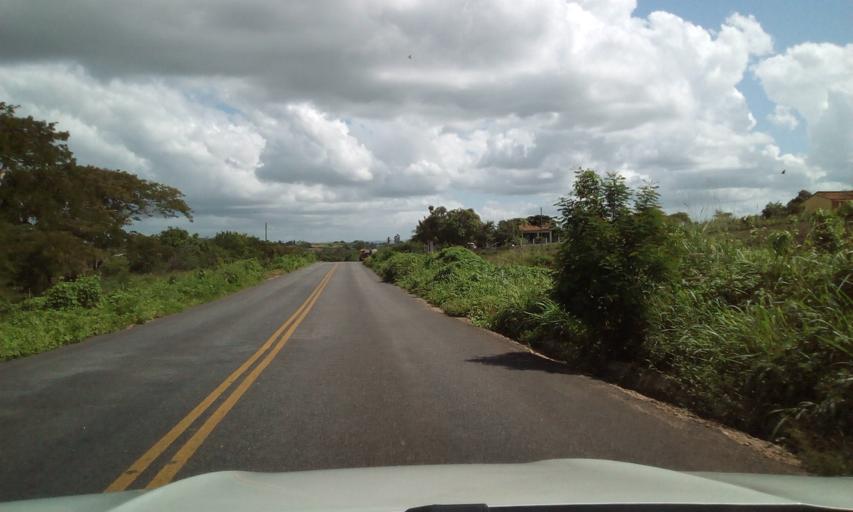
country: BR
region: Paraiba
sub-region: Guarabira
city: Guarabira
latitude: -6.8521
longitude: -35.3988
